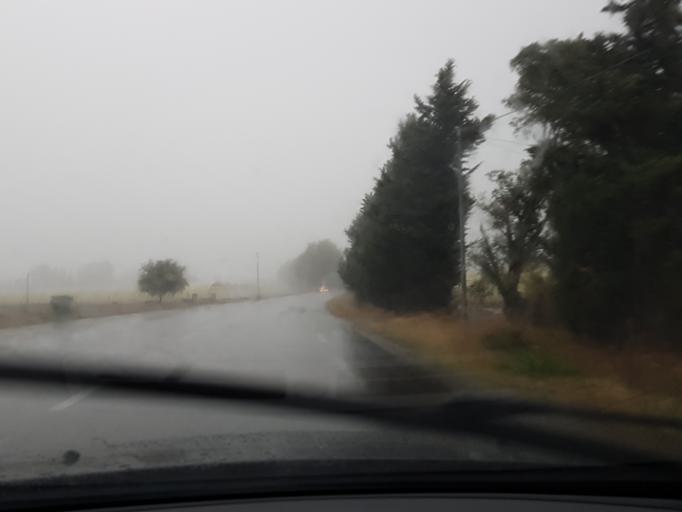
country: FR
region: Provence-Alpes-Cote d'Azur
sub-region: Departement du Vaucluse
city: Pernes-les-Fontaines
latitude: 44.0063
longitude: 5.0207
